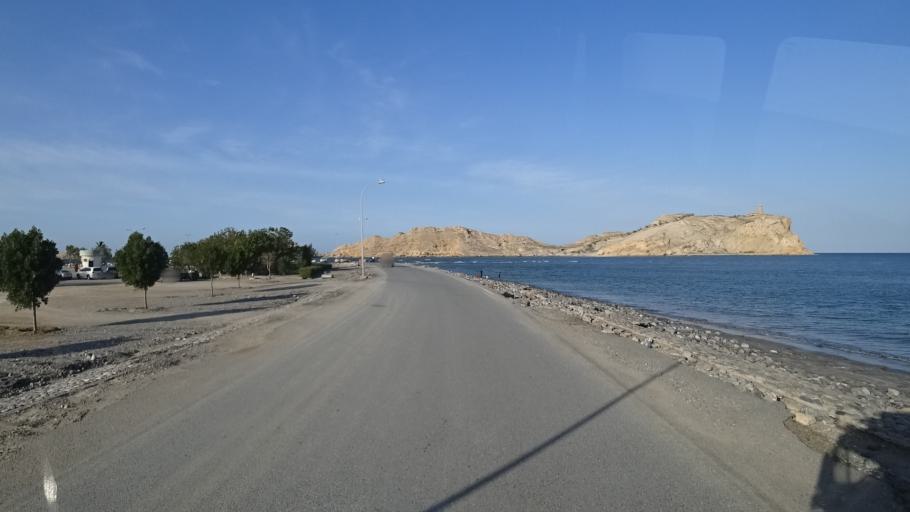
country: OM
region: Al Batinah
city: Barka'
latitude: 23.7798
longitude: 57.7906
